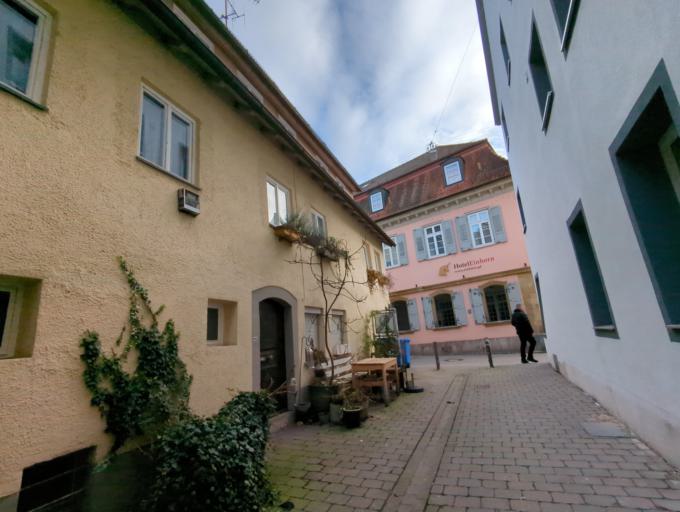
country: DE
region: Baden-Wuerttemberg
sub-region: Regierungsbezirk Stuttgart
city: Schwabisch Gmund
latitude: 48.7998
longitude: 9.7996
